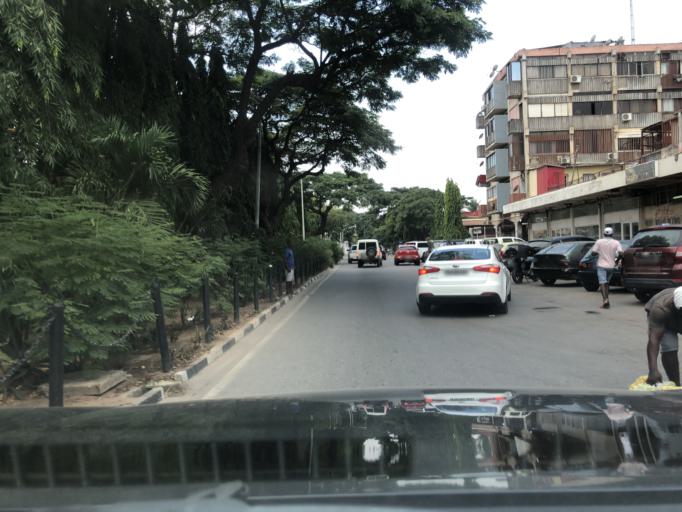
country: AO
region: Luanda
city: Luanda
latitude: -8.8263
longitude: 13.2477
